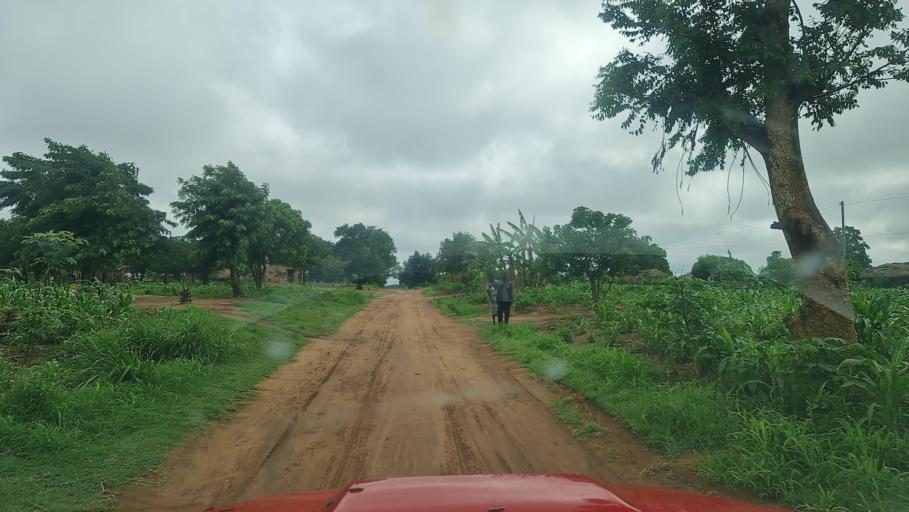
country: MW
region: Southern Region
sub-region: Nsanje District
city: Nsanje
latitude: -17.2045
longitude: 35.6837
